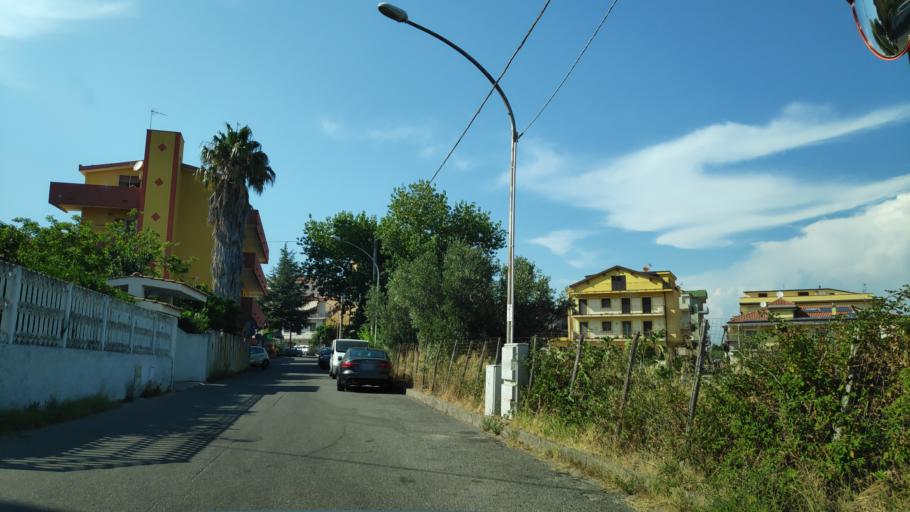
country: IT
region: Calabria
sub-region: Provincia di Catanzaro
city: Soverato Superiore
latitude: 38.6887
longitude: 16.5345
